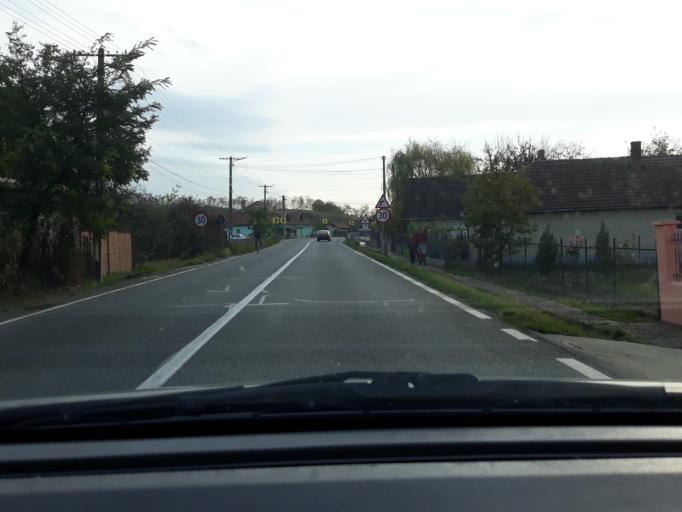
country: RO
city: Szekelyhid
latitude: 47.3389
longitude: 22.0915
